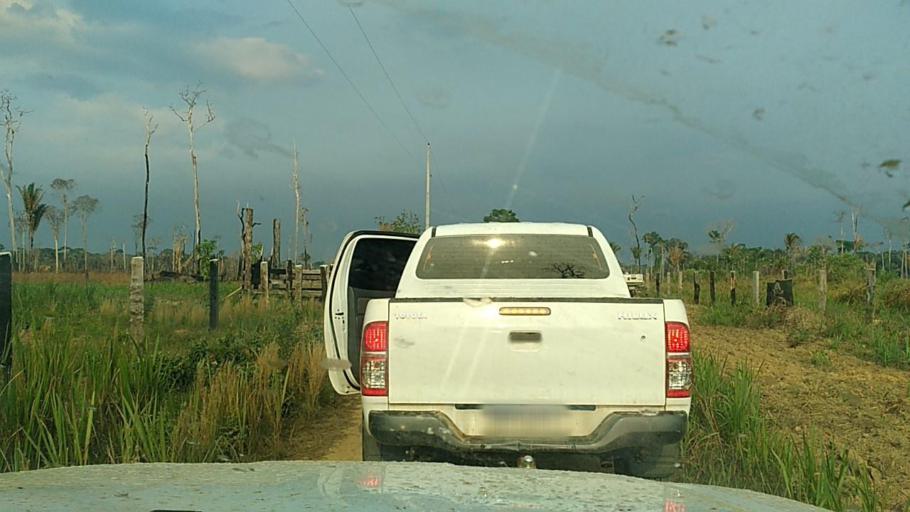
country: BR
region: Rondonia
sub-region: Porto Velho
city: Porto Velho
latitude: -8.5627
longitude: -64.0475
